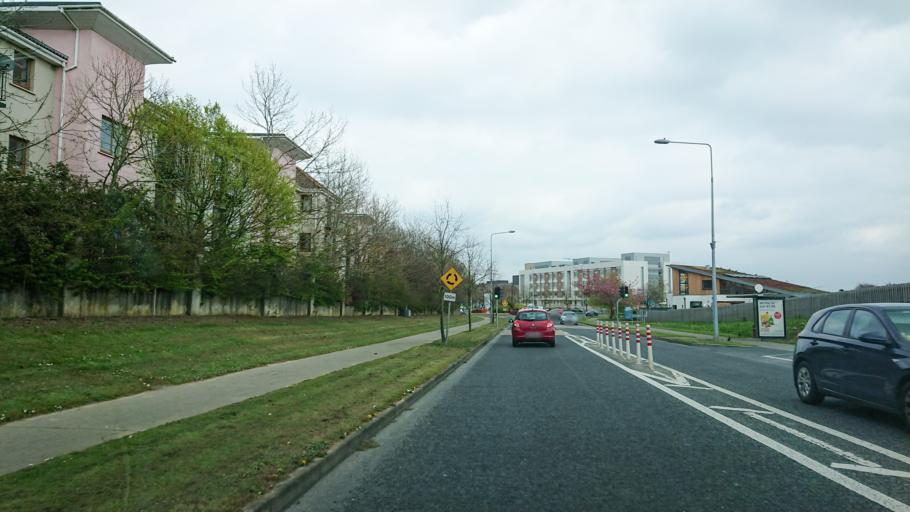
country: IE
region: Munster
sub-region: Waterford
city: Waterford
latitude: 52.2458
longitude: -7.0807
